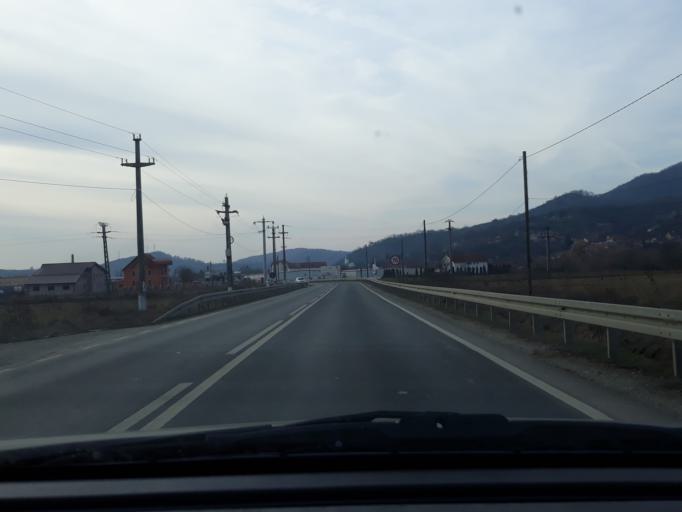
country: RO
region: Salaj
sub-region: Oras Simleu Silvaniei
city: Simleu Silvaniei
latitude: 47.2303
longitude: 22.8223
